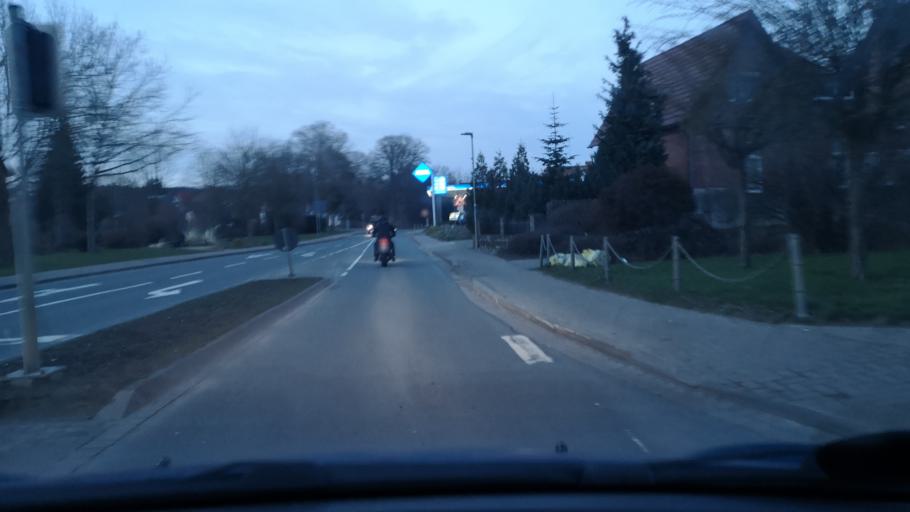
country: DE
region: Lower Saxony
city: Salzhemmendorf
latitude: 52.0671
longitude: 9.5850
